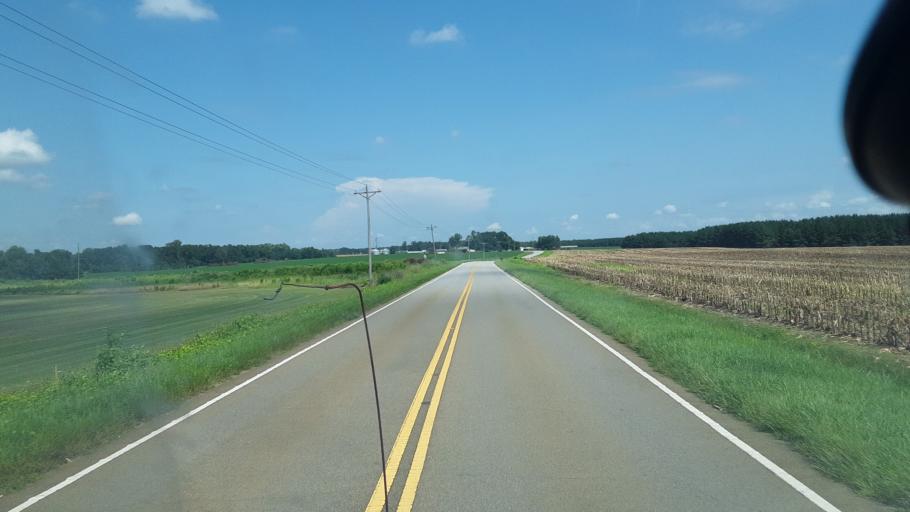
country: US
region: South Carolina
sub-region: Orangeburg County
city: Edisto
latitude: 33.4326
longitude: -81.0174
